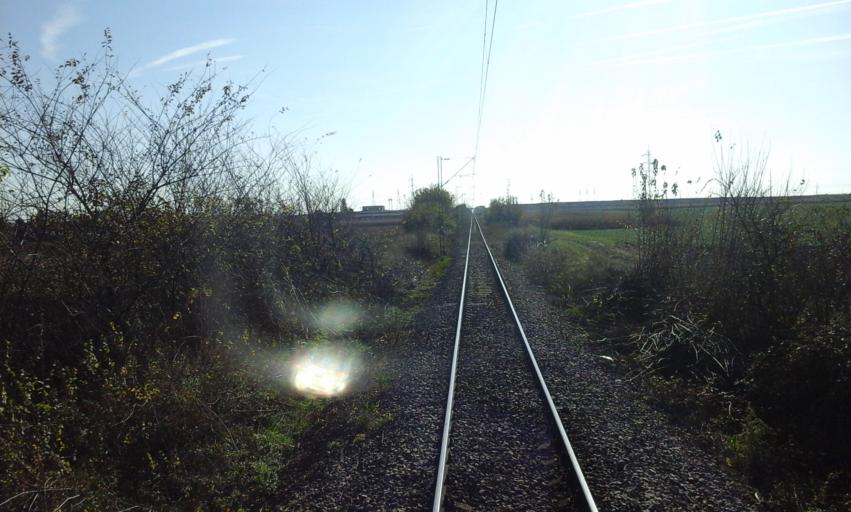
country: RS
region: Autonomna Pokrajina Vojvodina
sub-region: Severnobacki Okrug
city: Subotica
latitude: 46.0422
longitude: 19.6840
